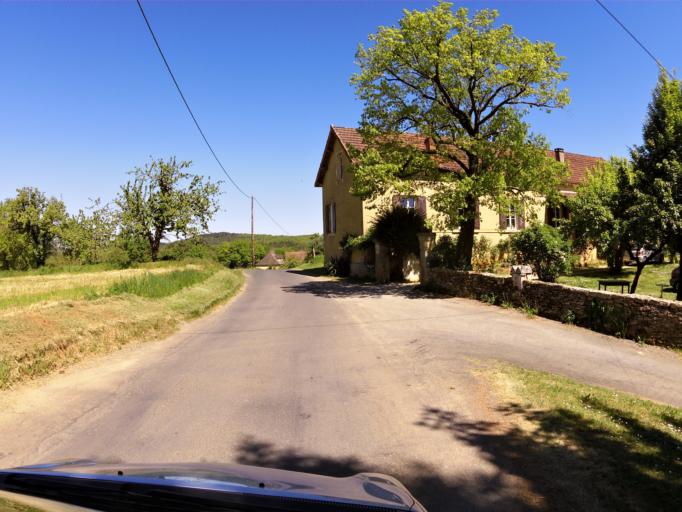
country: FR
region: Aquitaine
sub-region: Departement de la Dordogne
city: Eyvigues-et-Eybenes
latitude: 44.9266
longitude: 1.3056
